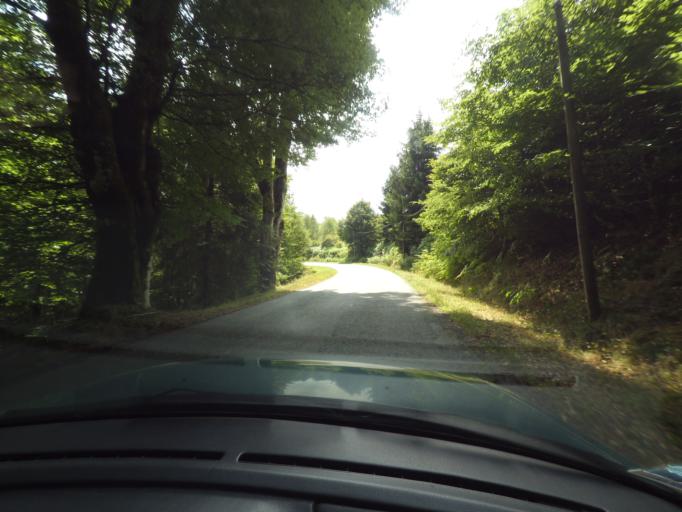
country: FR
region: Limousin
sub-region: Departement de la Correze
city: Bugeat
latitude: 45.7506
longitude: 1.9571
